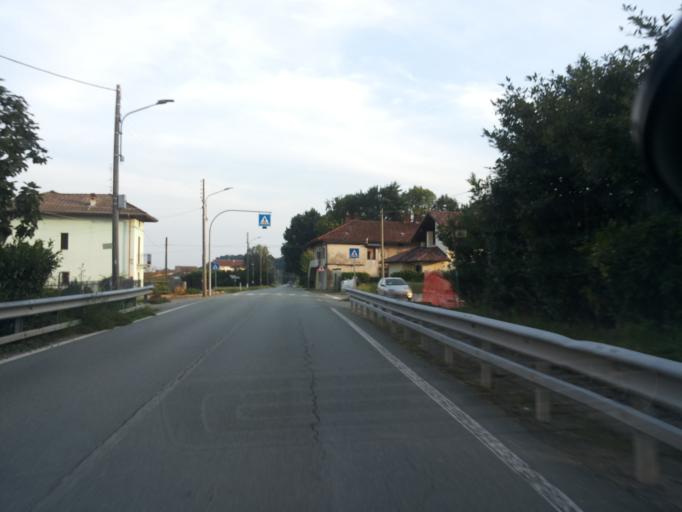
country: IT
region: Piedmont
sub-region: Provincia di Biella
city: Mottalciata
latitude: 45.5219
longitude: 8.1985
